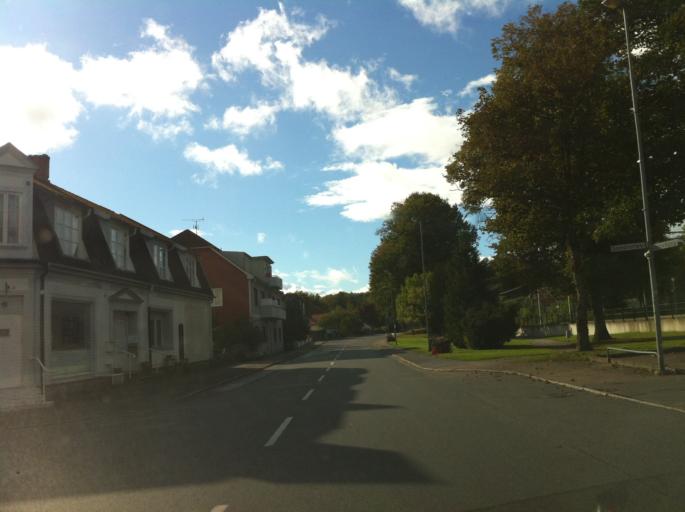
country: SE
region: Skane
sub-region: Hassleholms Kommun
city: Tormestorp
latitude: 56.1594
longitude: 13.5977
